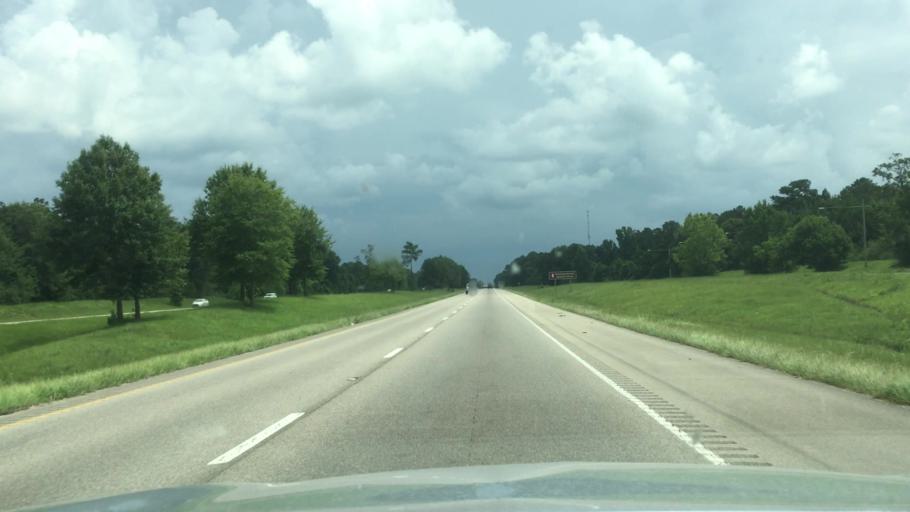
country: US
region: Mississippi
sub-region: Pearl River County
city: Picayune
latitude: 30.5624
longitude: -89.6389
